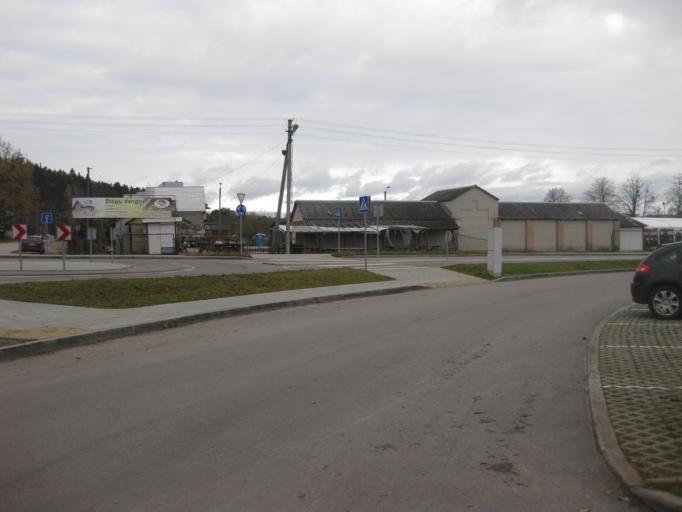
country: LT
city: Prienai
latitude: 54.6428
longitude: 23.9438
